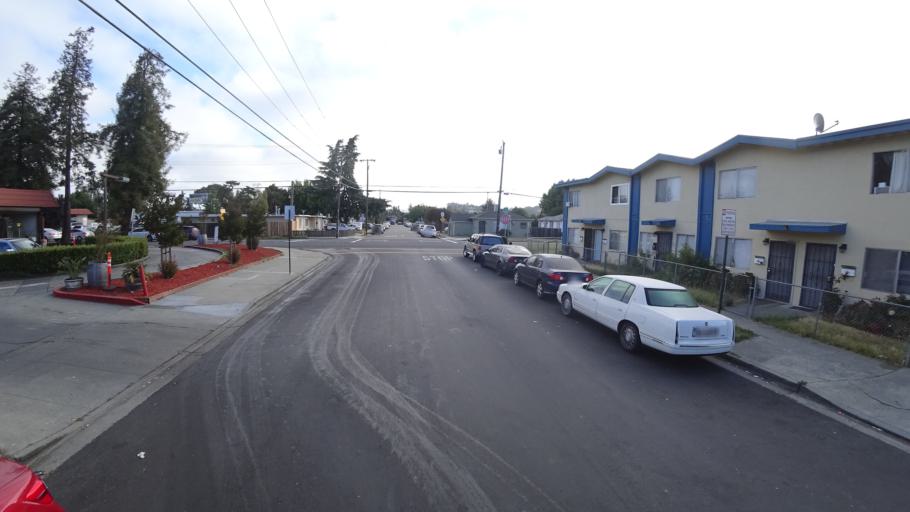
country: US
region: California
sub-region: Alameda County
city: Hayward
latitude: 37.6575
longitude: -122.0858
